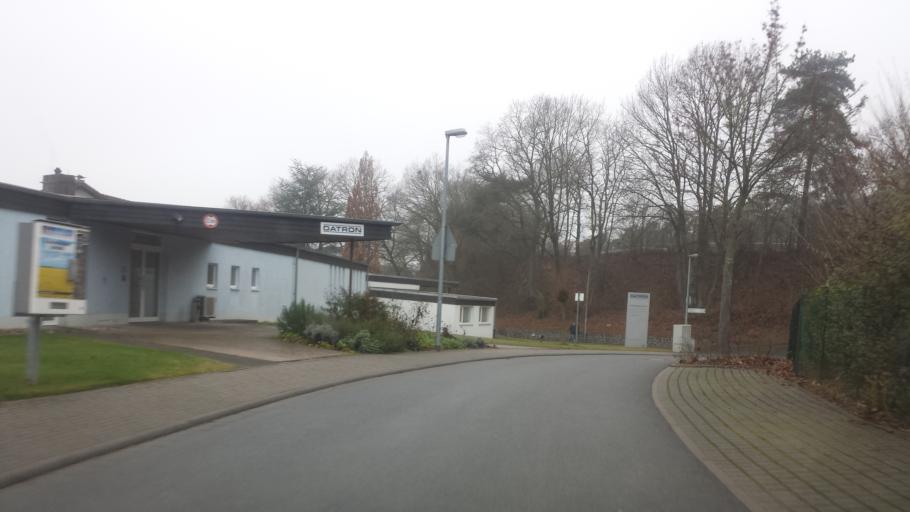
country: DE
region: Hesse
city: Ober-Ramstadt
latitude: 49.8437
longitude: 8.7117
